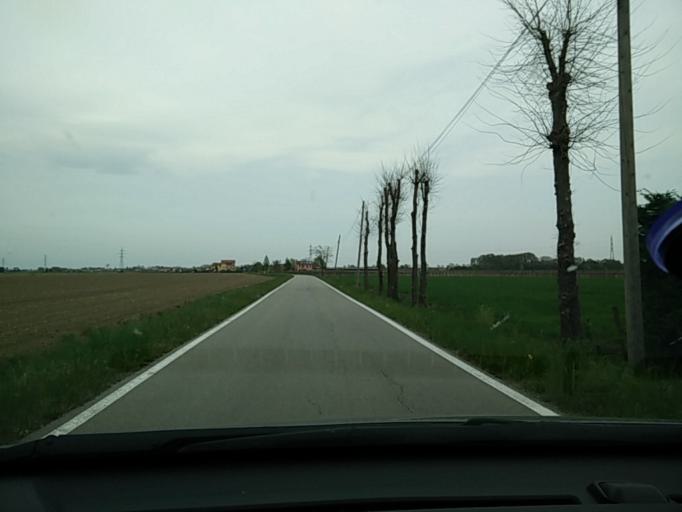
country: IT
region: Veneto
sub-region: Provincia di Treviso
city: Zenson di Piave
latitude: 45.6550
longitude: 12.4771
